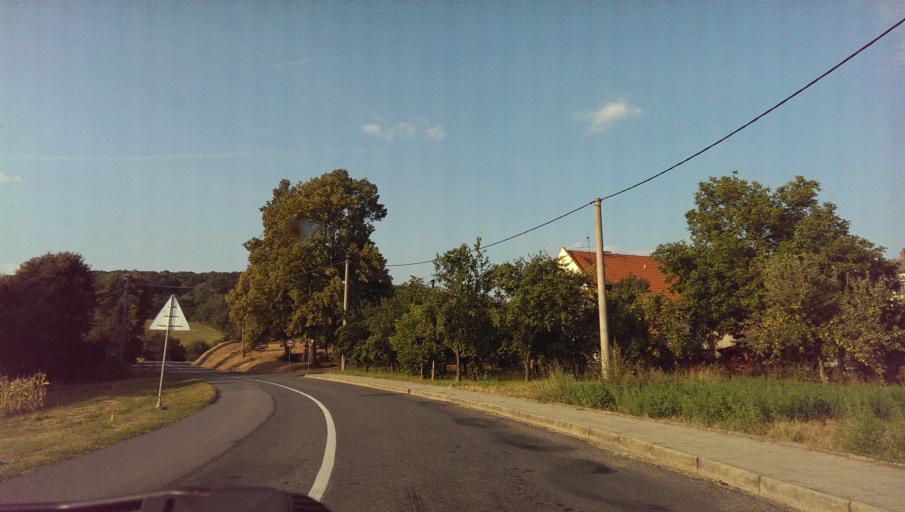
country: CZ
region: Zlin
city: Polesovice
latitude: 49.0542
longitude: 17.3038
